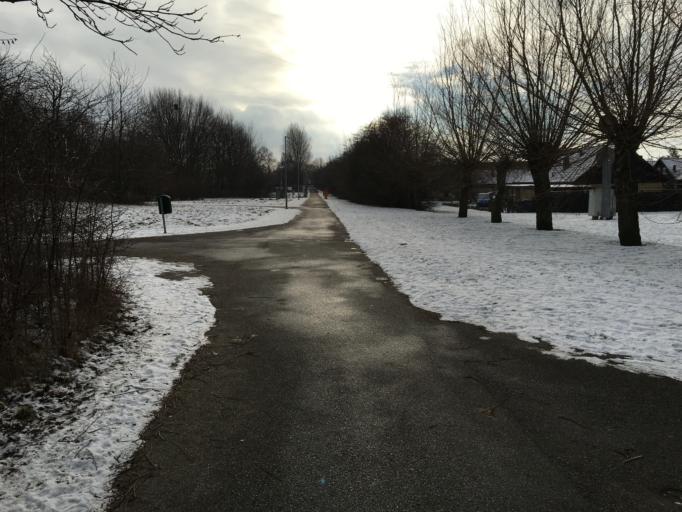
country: SE
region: Skane
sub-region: Vellinge Kommun
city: Vellinge
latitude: 55.4773
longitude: 13.0337
